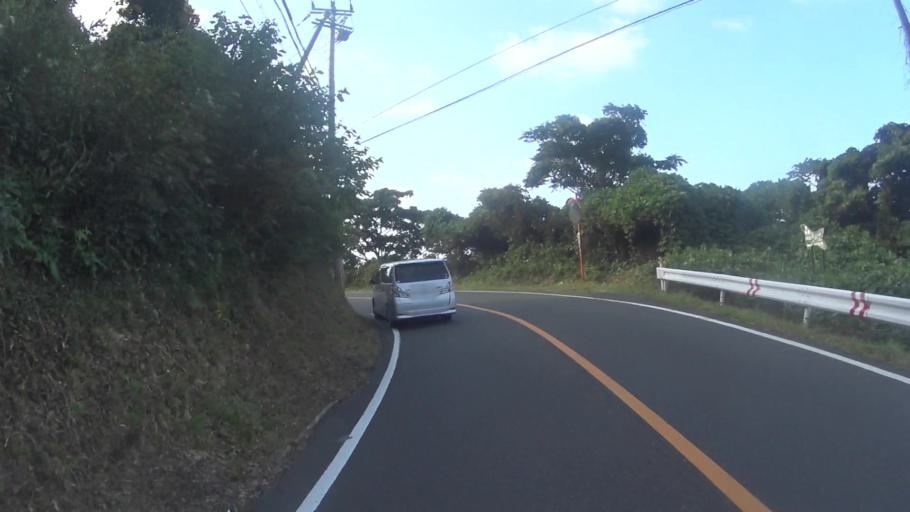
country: JP
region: Kyoto
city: Miyazu
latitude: 35.7519
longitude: 135.1569
